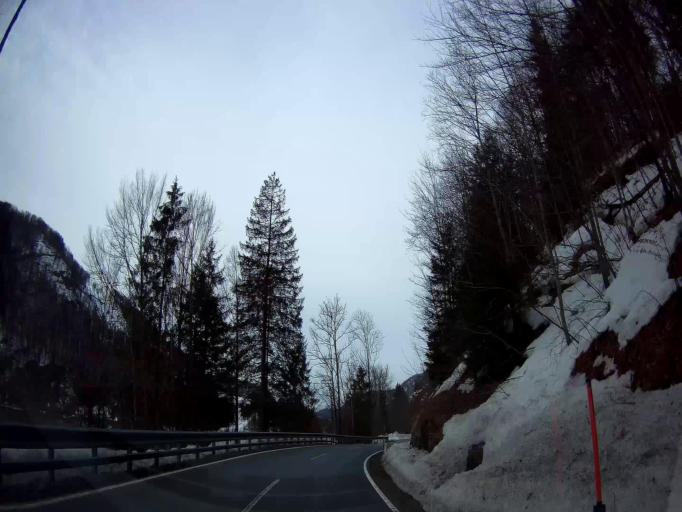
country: AT
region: Salzburg
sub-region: Politischer Bezirk Salzburg-Umgebung
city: Ebenau
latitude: 47.7549
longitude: 13.1789
